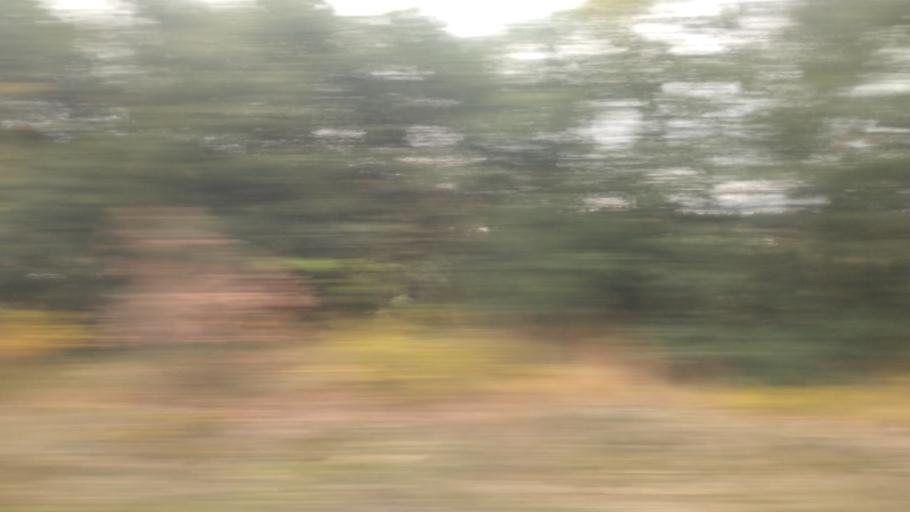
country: JP
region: Gifu
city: Tajimi
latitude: 35.3510
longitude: 137.1355
